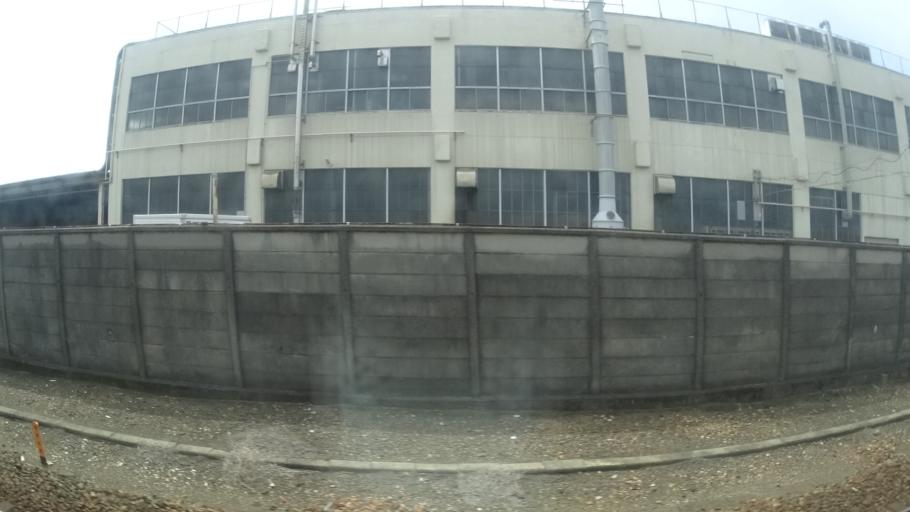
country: JP
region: Shizuoka
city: Hamamatsu
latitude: 34.6905
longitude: 137.6753
